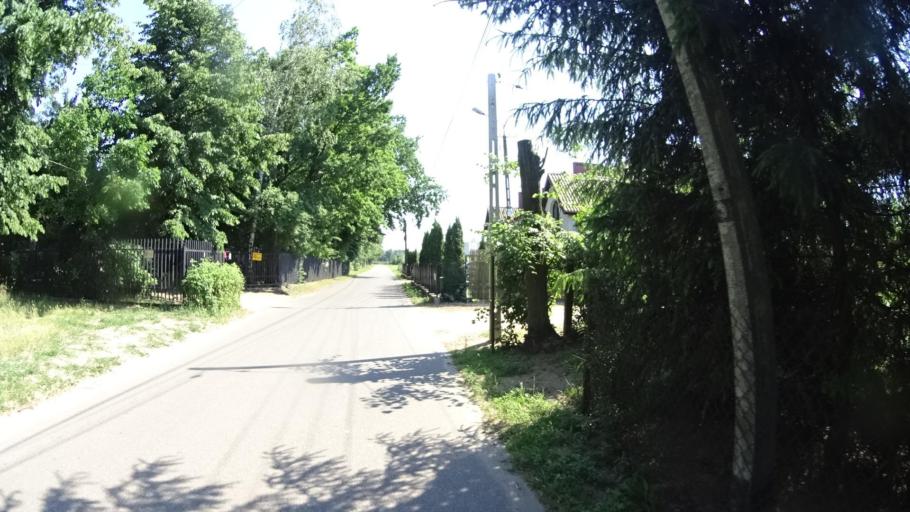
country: PL
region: Masovian Voivodeship
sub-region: Powiat warszawski zachodni
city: Bieniewice
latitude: 52.1895
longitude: 20.5507
